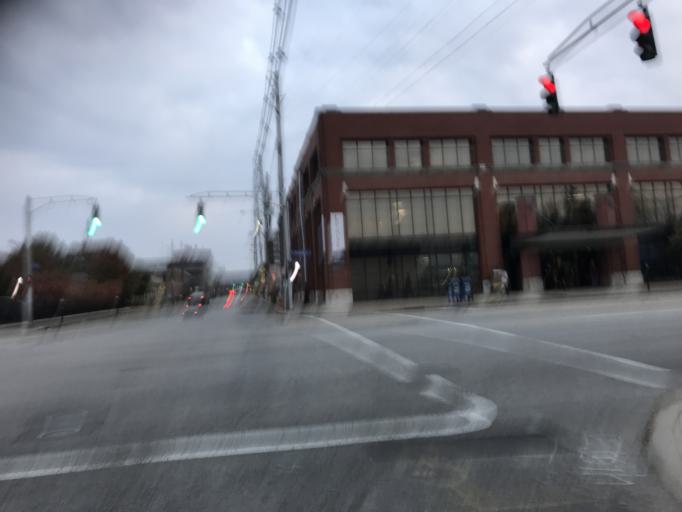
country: US
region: Kentucky
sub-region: Jefferson County
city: Louisville
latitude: 38.2450
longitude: -85.7456
